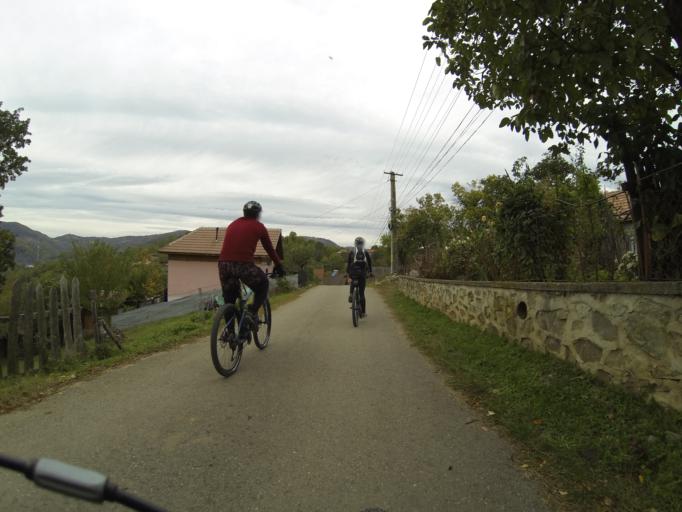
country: RO
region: Gorj
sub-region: Comuna Tismana
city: Sohodol
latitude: 45.0526
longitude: 22.8970
